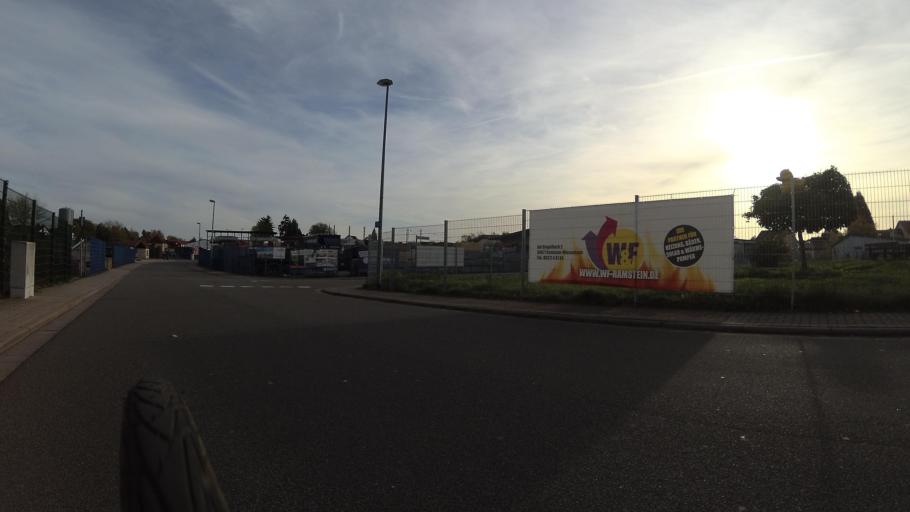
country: DE
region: Rheinland-Pfalz
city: Ramstein-Miesenbach
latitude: 49.4518
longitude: 7.5542
